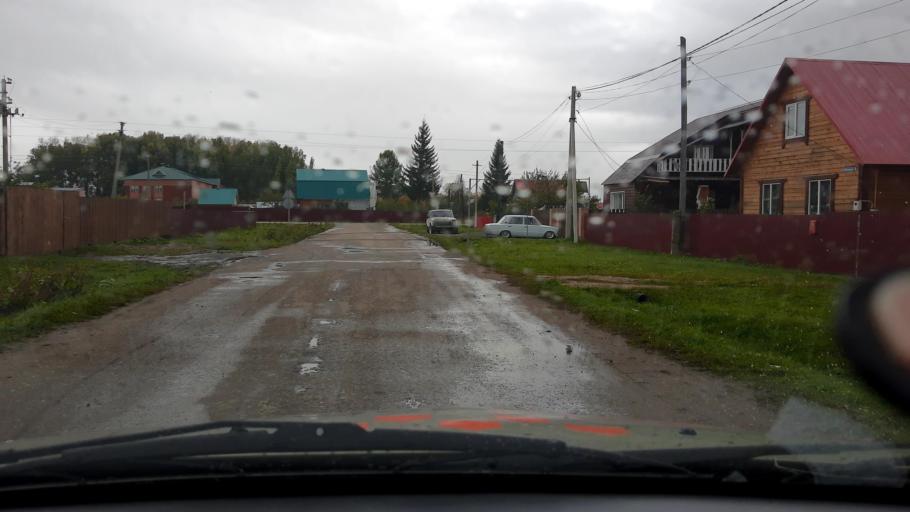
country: RU
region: Bashkortostan
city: Kudeyevskiy
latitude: 54.8801
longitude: 56.6427
